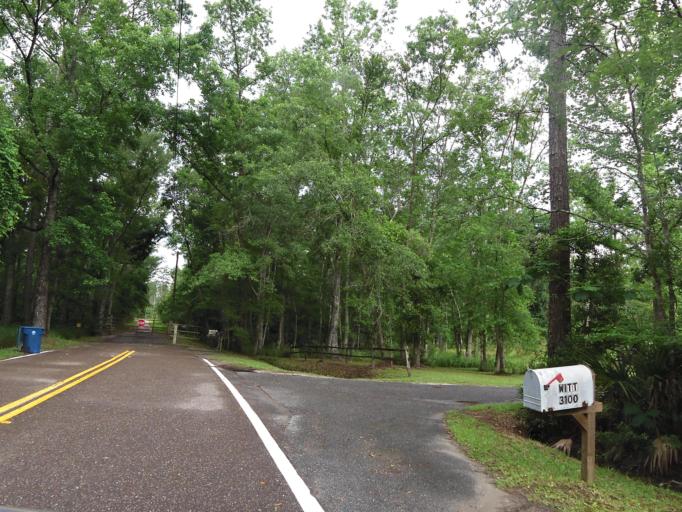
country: US
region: Florida
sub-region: Nassau County
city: Yulee
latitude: 30.5465
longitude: -81.6900
